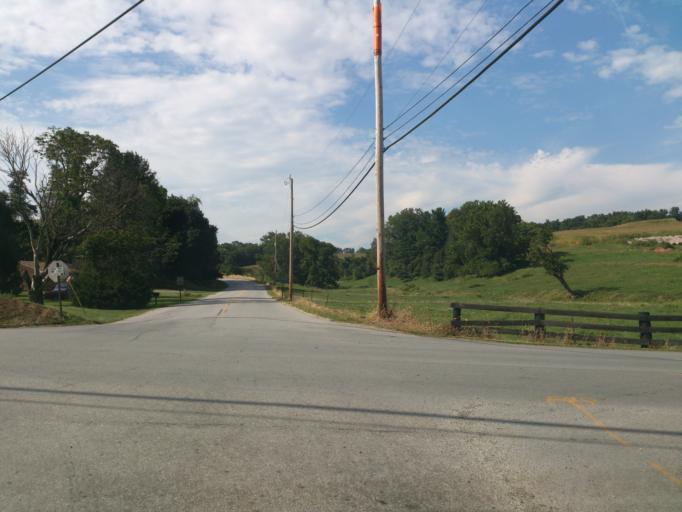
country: US
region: Pennsylvania
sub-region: York County
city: Wrightsville
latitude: 39.9652
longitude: -76.5367
